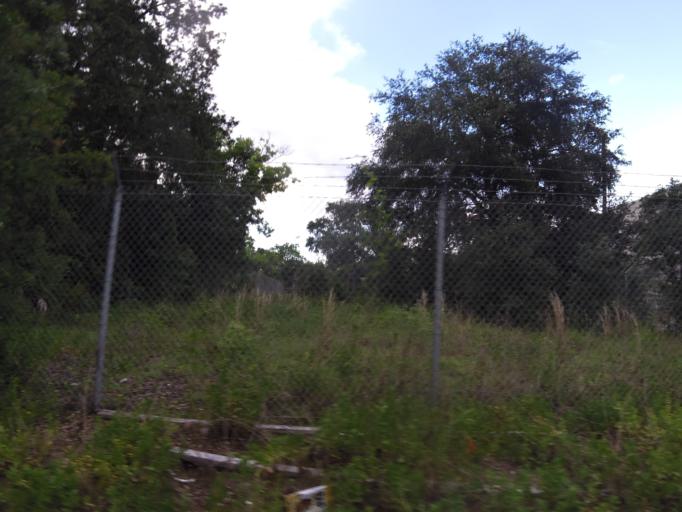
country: US
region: Florida
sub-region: Duval County
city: Jacksonville
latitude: 30.3251
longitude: -81.6706
